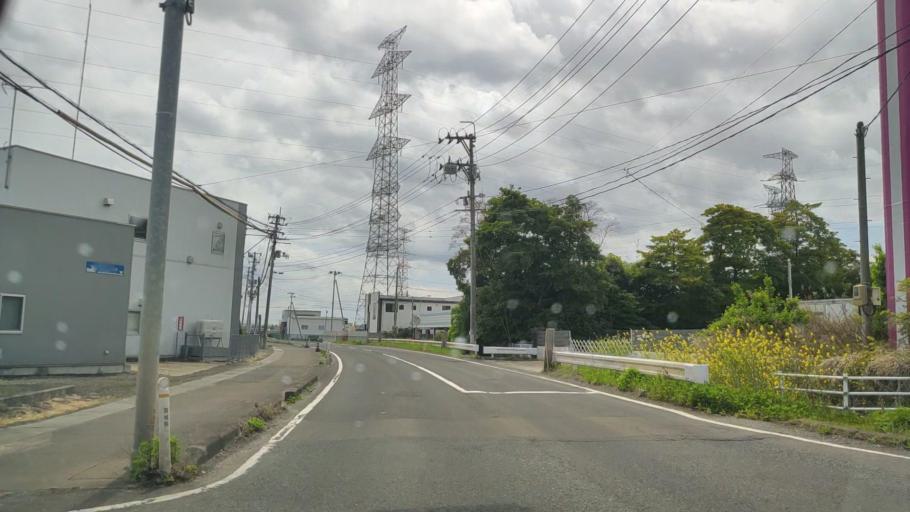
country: JP
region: Miyagi
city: Shiogama
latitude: 38.2830
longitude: 141.0070
